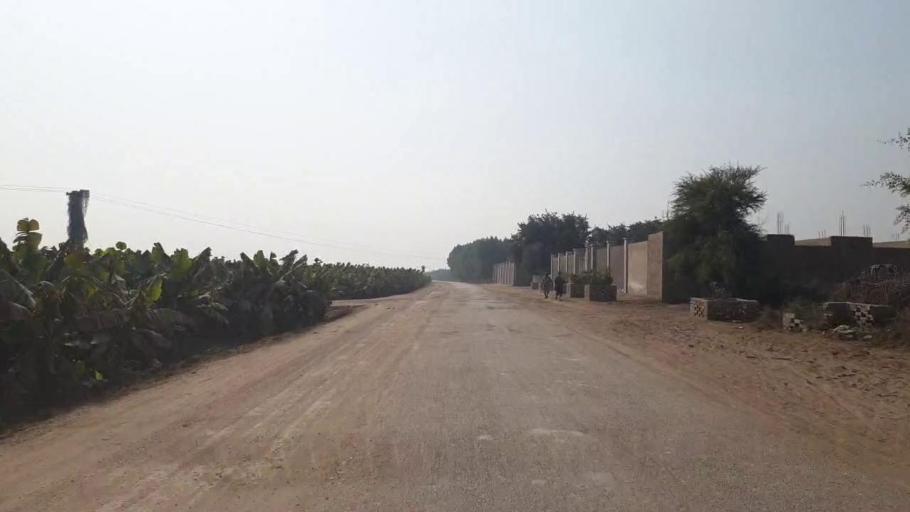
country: PK
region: Sindh
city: Hala
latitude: 25.9023
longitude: 68.4449
